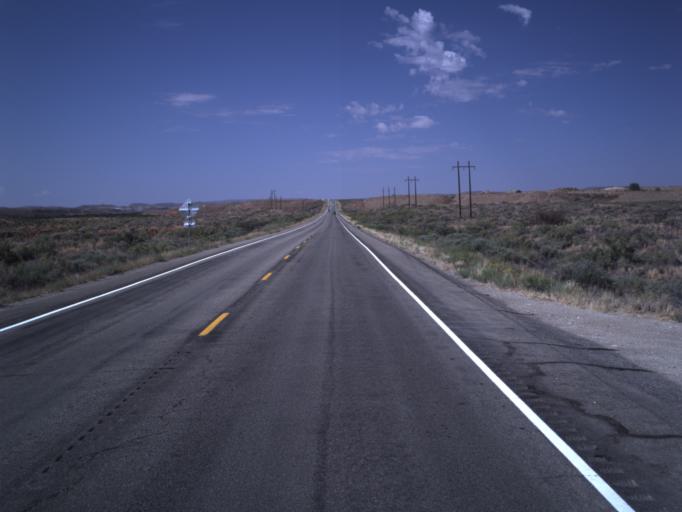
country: US
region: Utah
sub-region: San Juan County
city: Blanding
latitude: 37.2788
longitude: -109.5795
